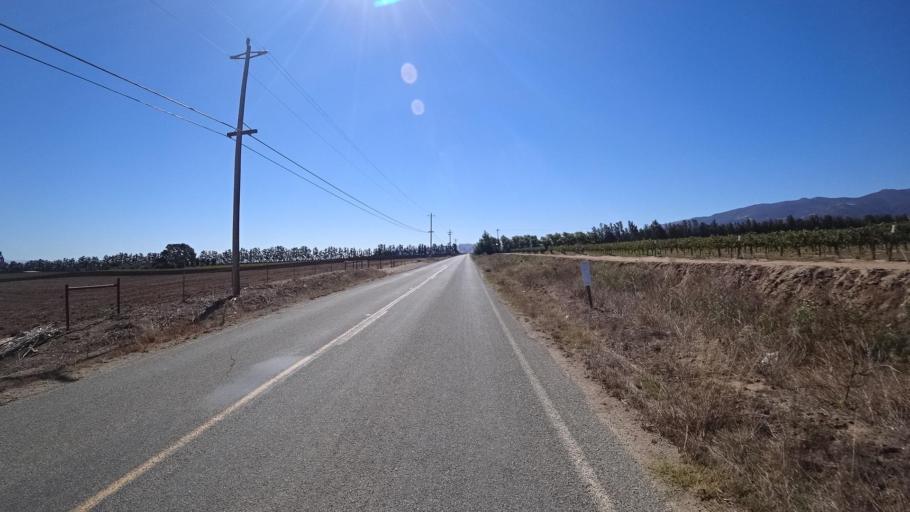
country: US
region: California
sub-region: Monterey County
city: Soledad
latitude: 36.3692
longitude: -121.3243
